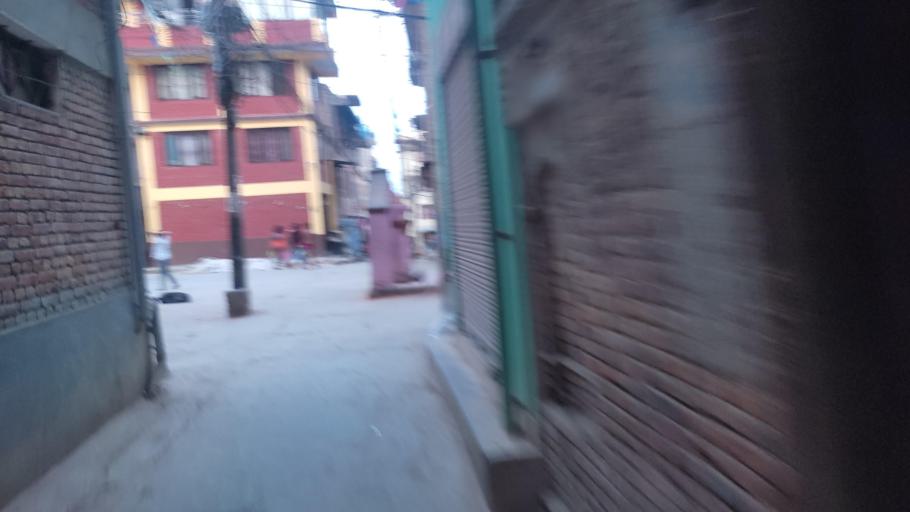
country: NP
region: Central Region
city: Kirtipur
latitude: 27.6692
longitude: 85.2764
